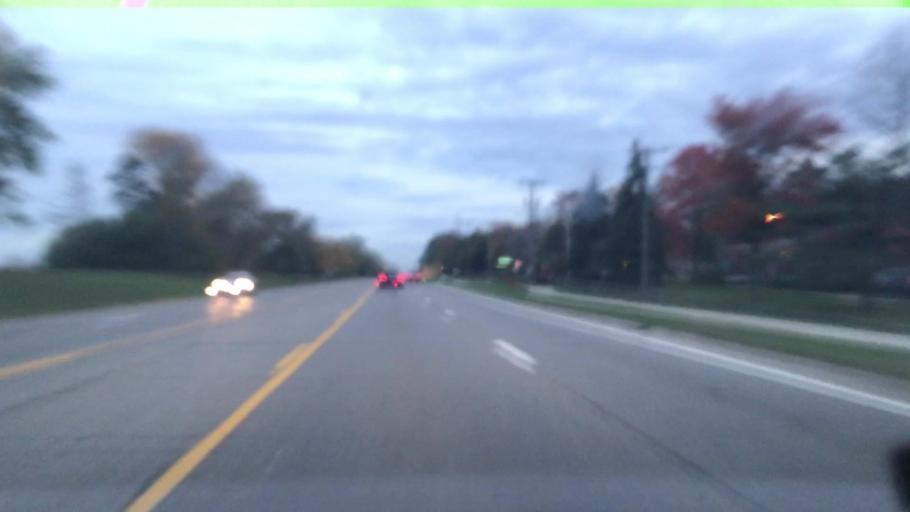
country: US
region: Michigan
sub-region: Oakland County
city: Bloomfield Hills
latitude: 42.6091
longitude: -83.2481
